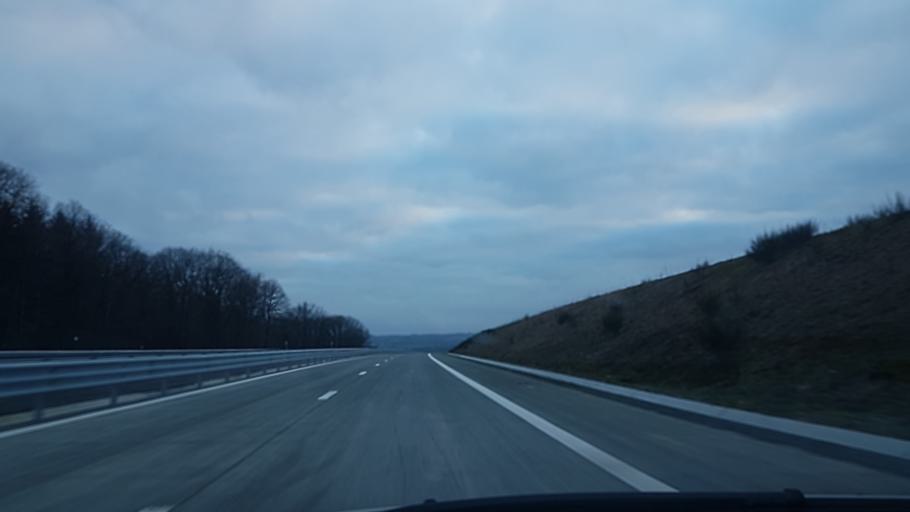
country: FR
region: Champagne-Ardenne
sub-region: Departement des Ardennes
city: Rocroi
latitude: 49.9923
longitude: 4.5424
